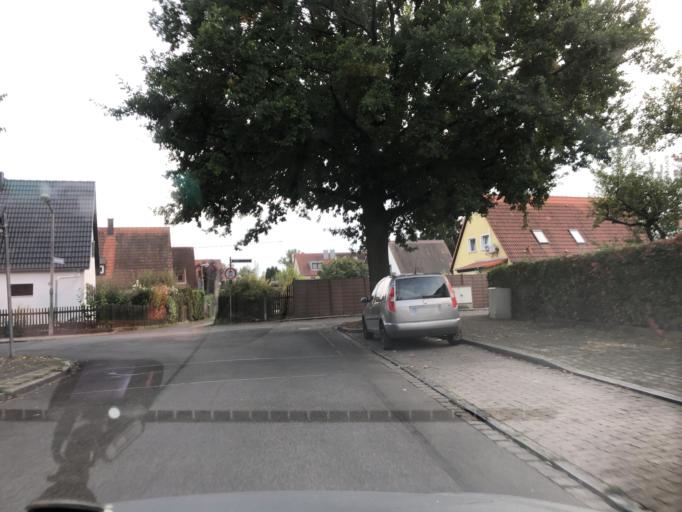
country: DE
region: Bavaria
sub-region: Regierungsbezirk Mittelfranken
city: Grossreuth bei Schweinau
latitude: 49.4416
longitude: 11.0069
